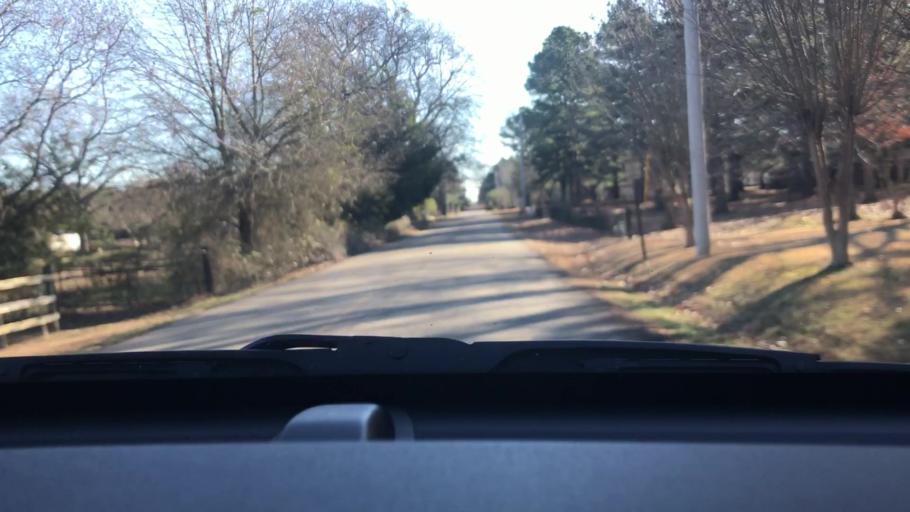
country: US
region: Arkansas
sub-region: Hempstead County
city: Hope
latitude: 33.6389
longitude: -93.5756
